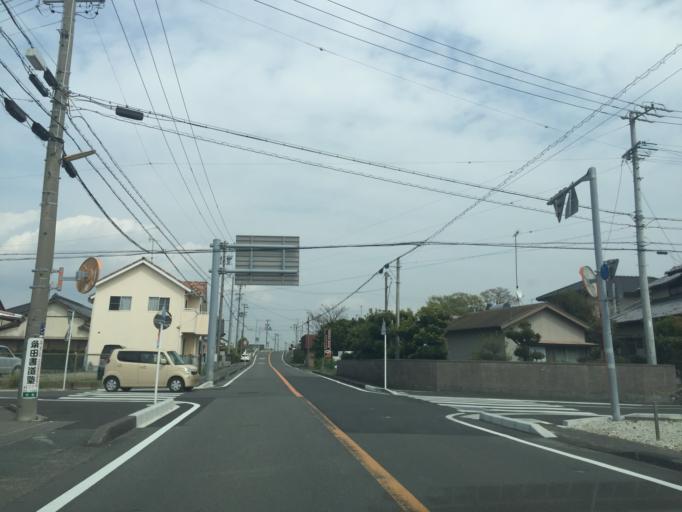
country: JP
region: Shizuoka
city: Kakegawa
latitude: 34.6764
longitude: 138.0480
